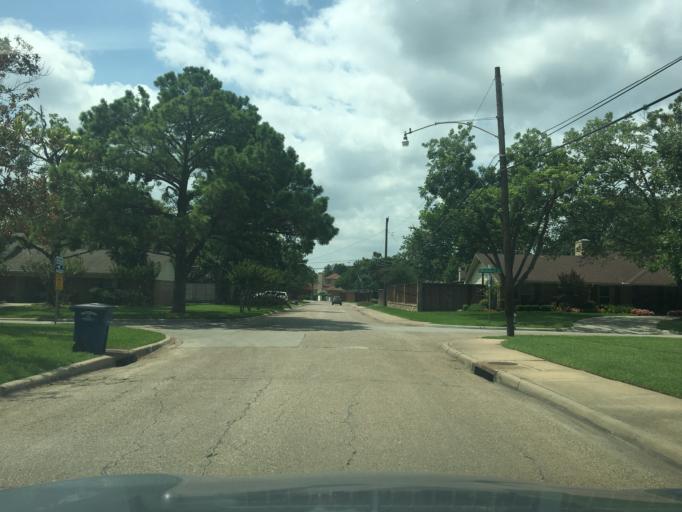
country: US
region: Texas
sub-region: Dallas County
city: Addison
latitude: 32.9163
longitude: -96.8237
